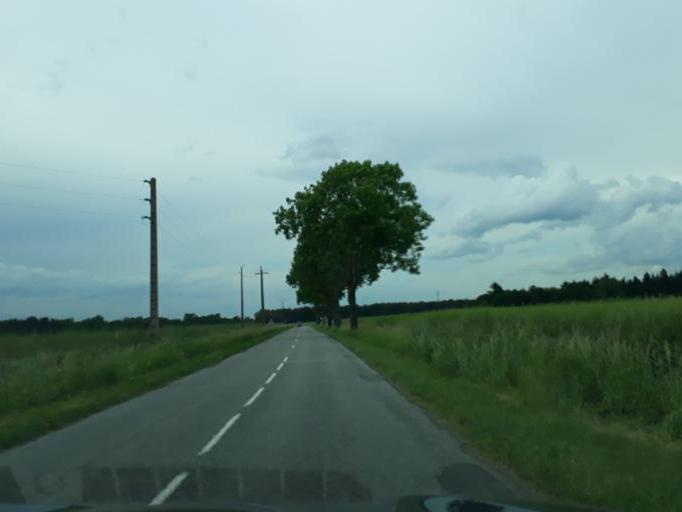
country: FR
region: Centre
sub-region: Departement du Loiret
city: Jargeau
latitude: 47.8453
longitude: 2.1368
